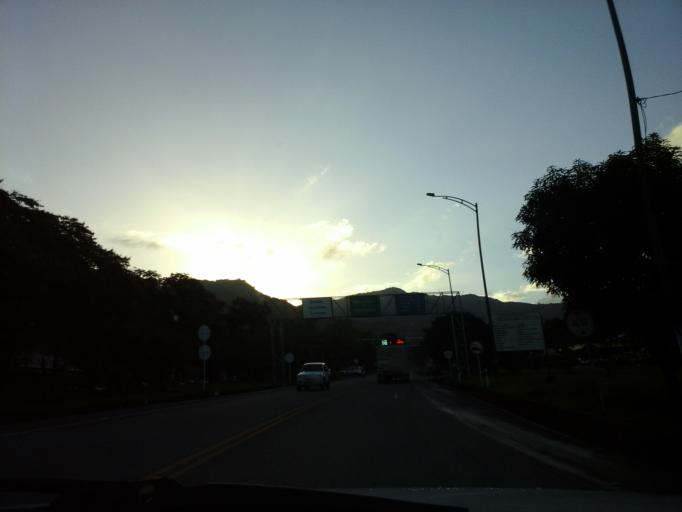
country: CO
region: Meta
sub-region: Villavicencio
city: Villavicencio
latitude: 4.1227
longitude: -73.6465
